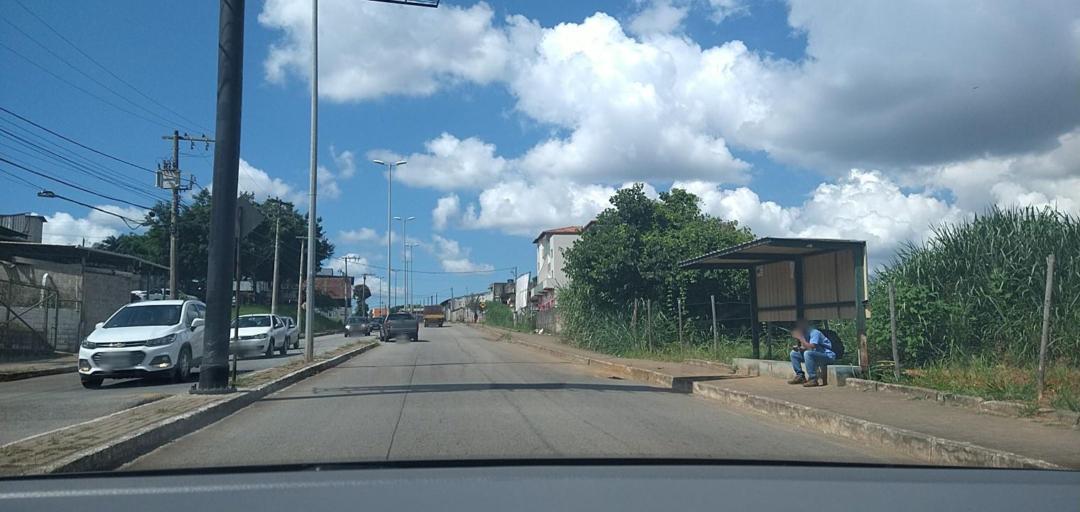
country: BR
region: Minas Gerais
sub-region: Joao Monlevade
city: Joao Monlevade
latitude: -19.8341
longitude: -43.1899
